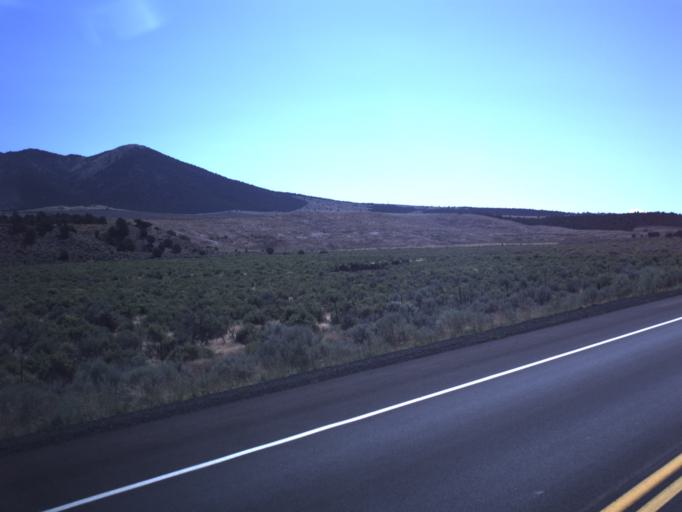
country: US
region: Utah
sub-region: Utah County
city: Eagle Mountain
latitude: 40.0148
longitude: -112.2780
